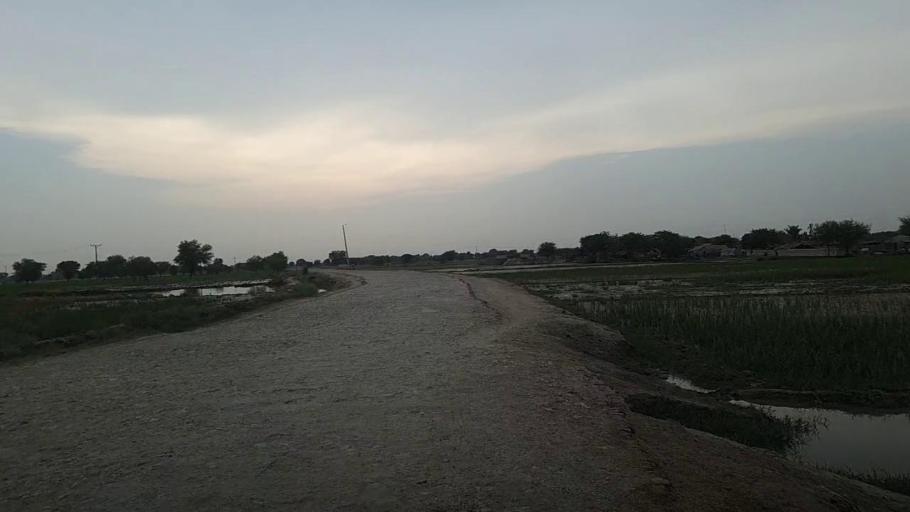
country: PK
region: Sindh
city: Khanpur
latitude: 27.8487
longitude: 69.4436
